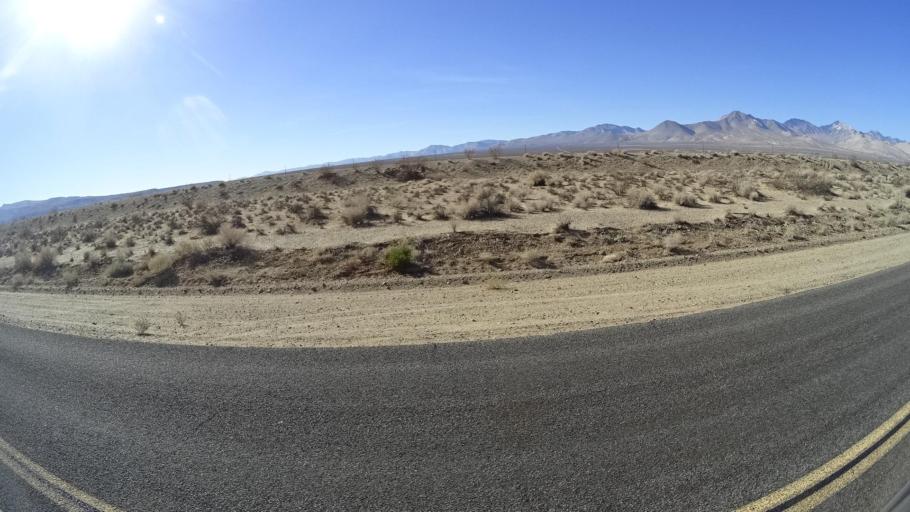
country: US
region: California
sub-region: Kern County
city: Inyokern
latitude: 35.6054
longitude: -117.7989
